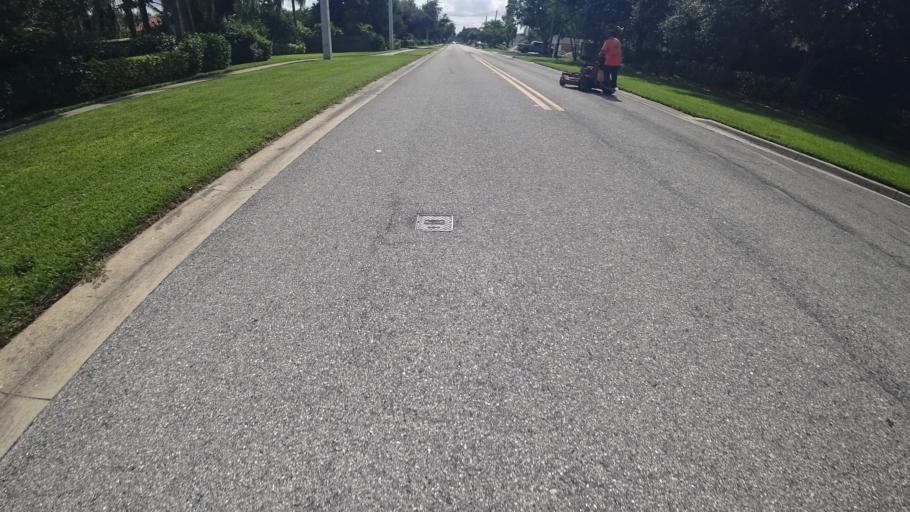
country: US
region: Florida
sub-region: Manatee County
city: West Bradenton
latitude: 27.5145
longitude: -82.6470
